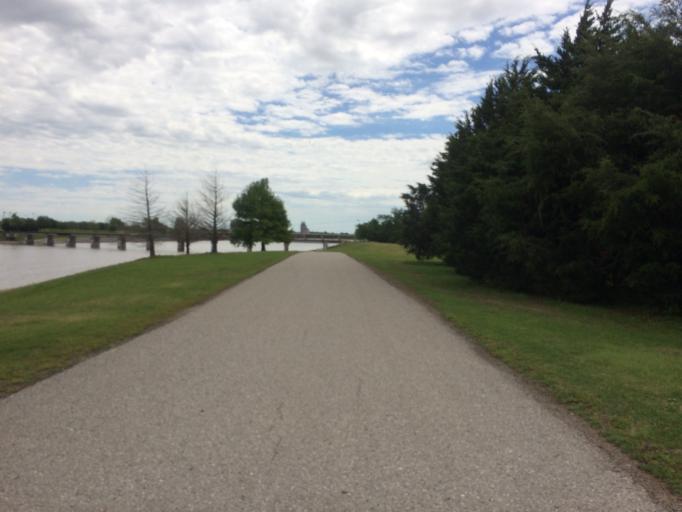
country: US
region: Oklahoma
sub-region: Oklahoma County
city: Oklahoma City
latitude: 35.4570
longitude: -97.5373
